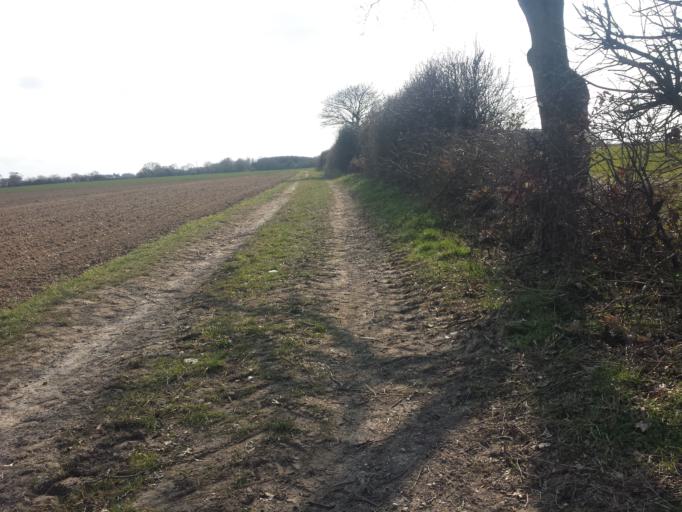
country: GB
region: England
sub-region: Essex
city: Little Clacton
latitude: 51.8931
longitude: 1.1628
